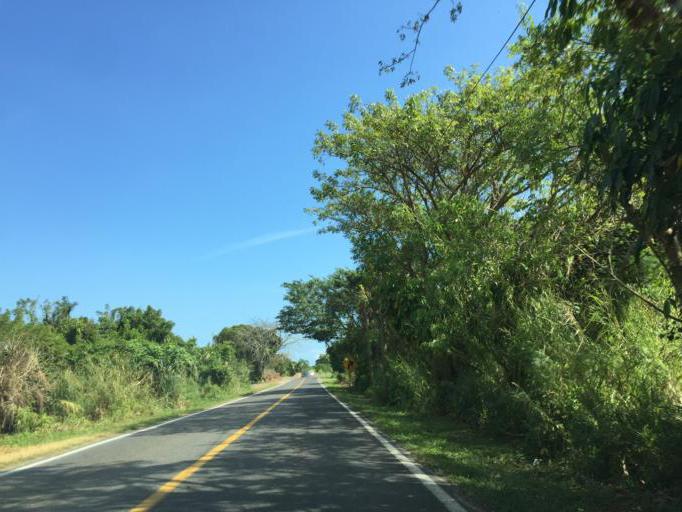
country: MX
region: Veracruz
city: Gutierrez Zamora
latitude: 20.4797
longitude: -97.0732
